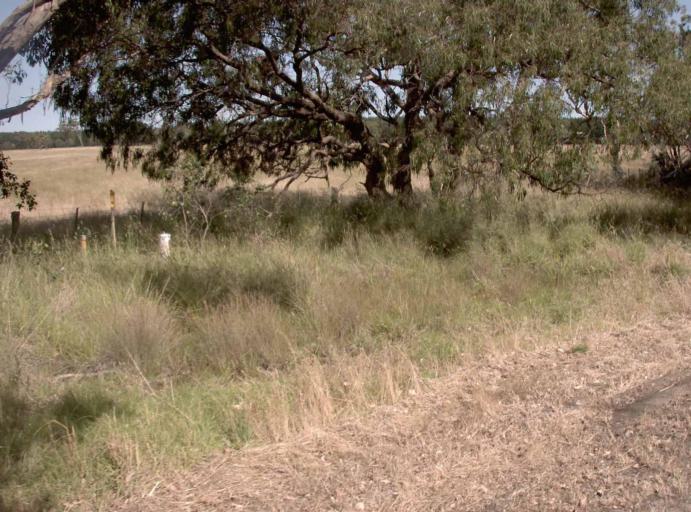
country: AU
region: Victoria
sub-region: Wellington
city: Sale
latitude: -38.2889
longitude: 147.1554
